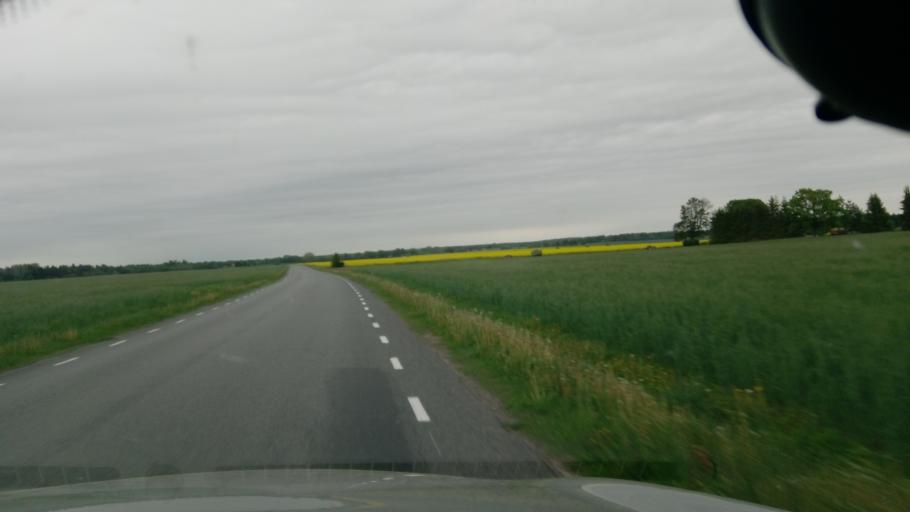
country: EE
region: Jaervamaa
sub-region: Koeru vald
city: Koeru
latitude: 58.9917
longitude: 26.0580
